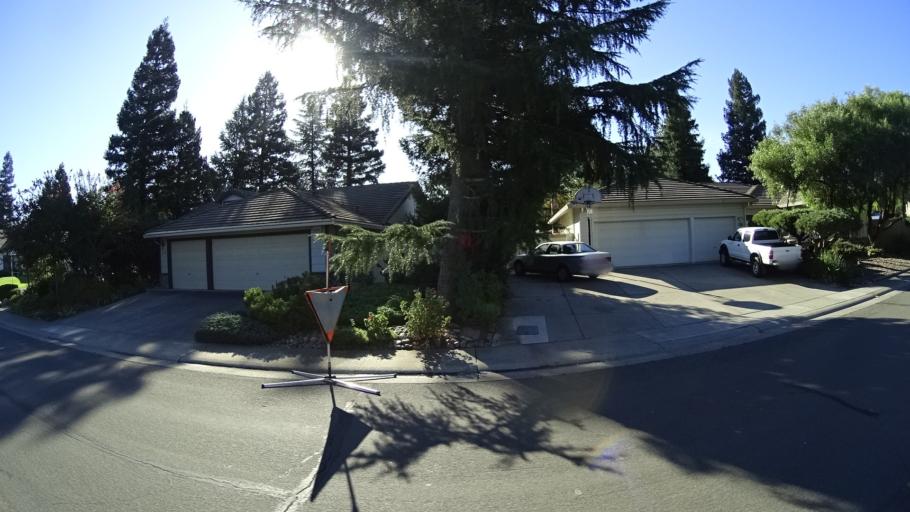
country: US
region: California
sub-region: Sacramento County
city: Elk Grove
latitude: 38.4319
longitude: -121.3790
